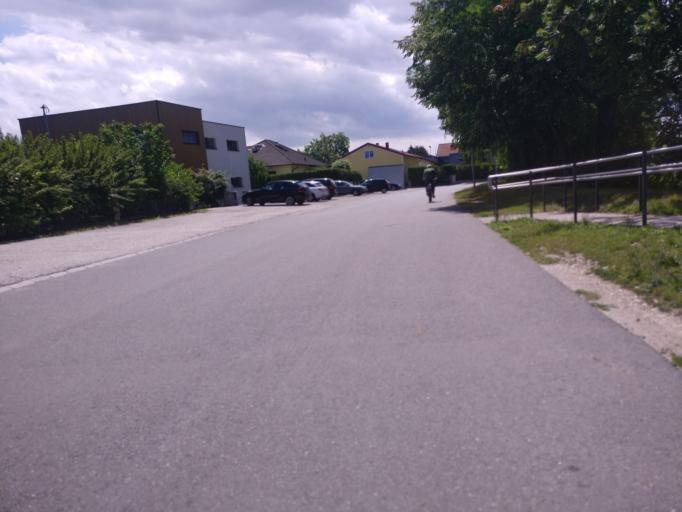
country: AT
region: Lower Austria
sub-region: Politischer Bezirk Baden
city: Ebreichsdorf
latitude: 47.9603
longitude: 16.4010
